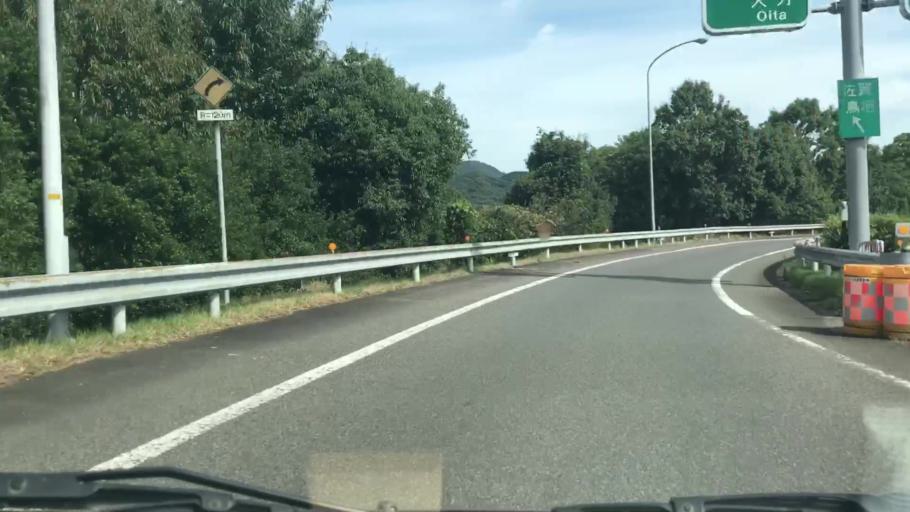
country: JP
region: Saga Prefecture
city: Takeocho-takeo
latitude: 33.2181
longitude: 130.0485
